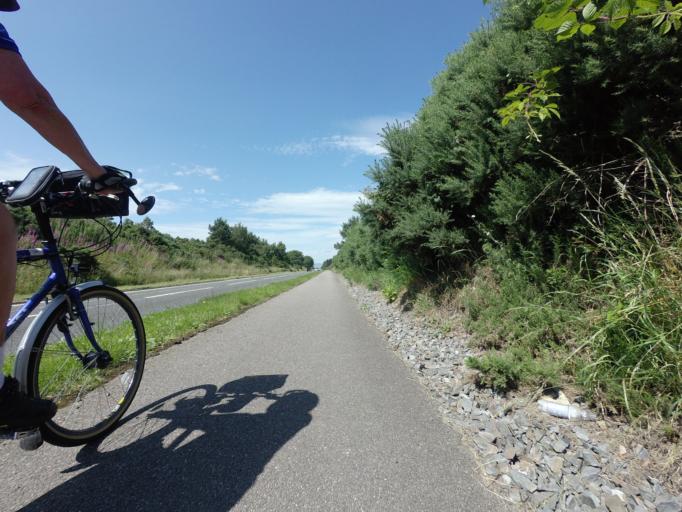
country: GB
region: Scotland
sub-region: Highland
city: Conon Bridge
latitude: 57.5432
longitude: -4.3790
